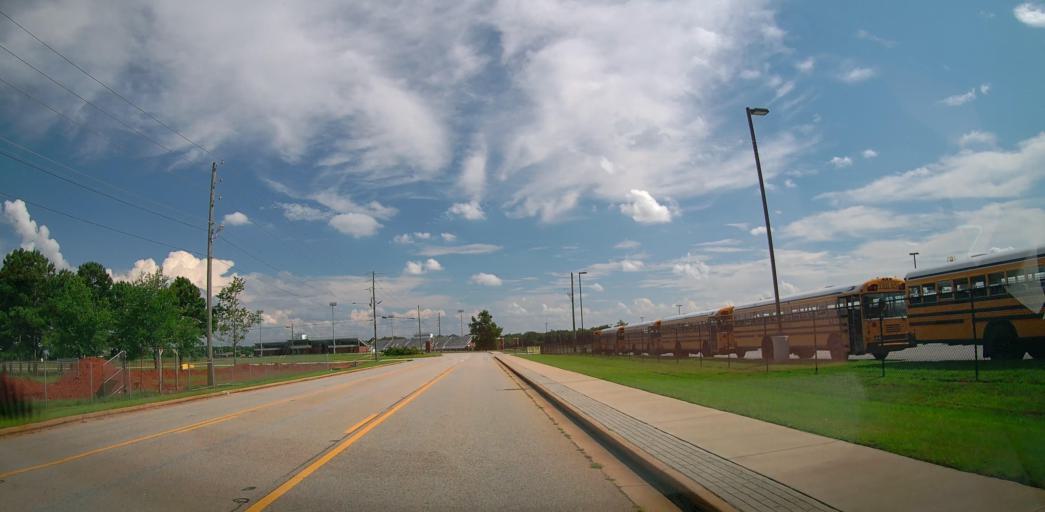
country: US
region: Georgia
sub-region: Houston County
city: Centerville
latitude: 32.5510
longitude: -83.6798
